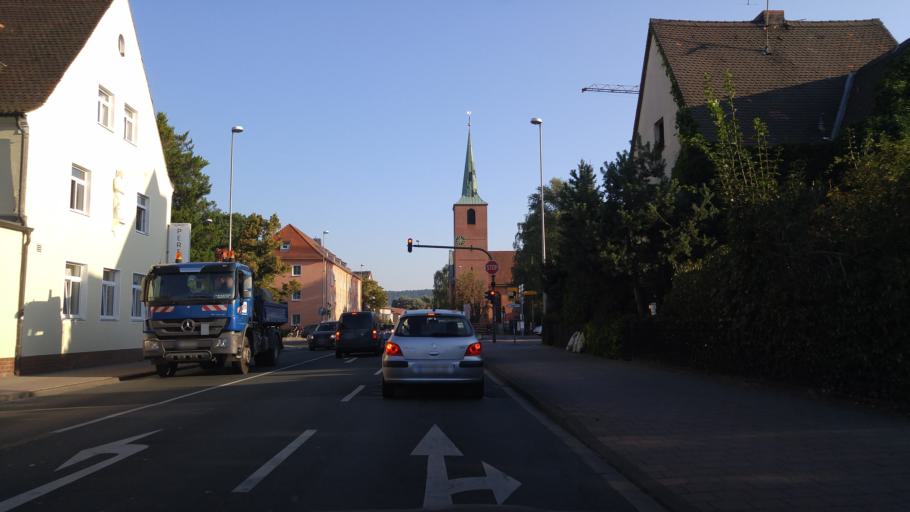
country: DE
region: Bavaria
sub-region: Regierungsbezirk Mittelfranken
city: Buckenhof
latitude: 49.5951
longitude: 11.0360
